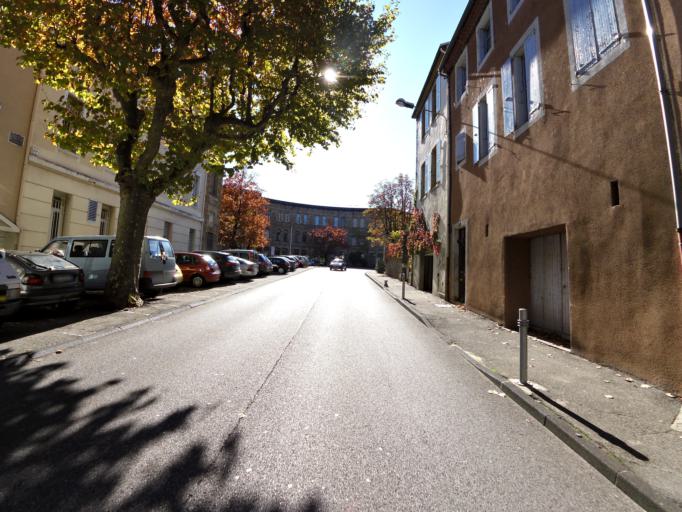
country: FR
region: Rhone-Alpes
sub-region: Departement de l'Ardeche
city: Privas
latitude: 44.7336
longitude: 4.5938
